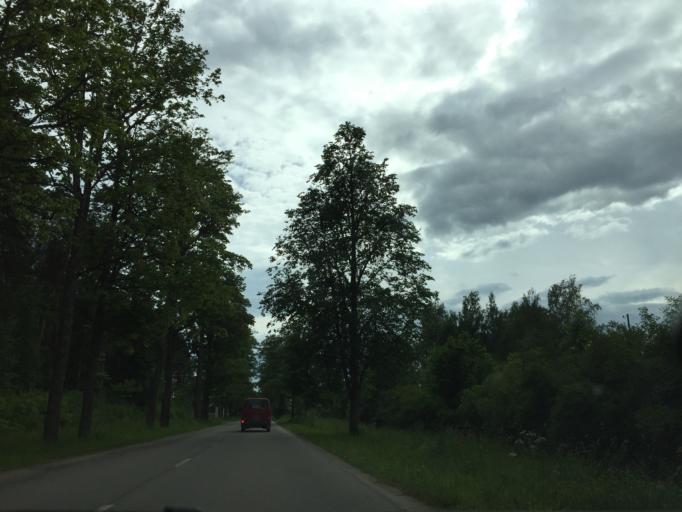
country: LV
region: Apes Novads
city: Ape
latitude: 57.5100
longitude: 26.4023
